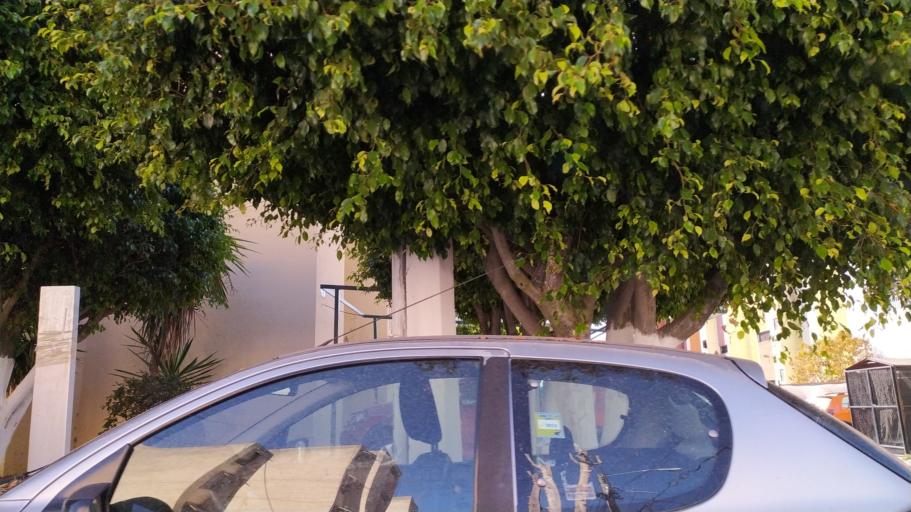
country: MX
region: Jalisco
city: Guadalajara
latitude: 20.6554
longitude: -103.4307
